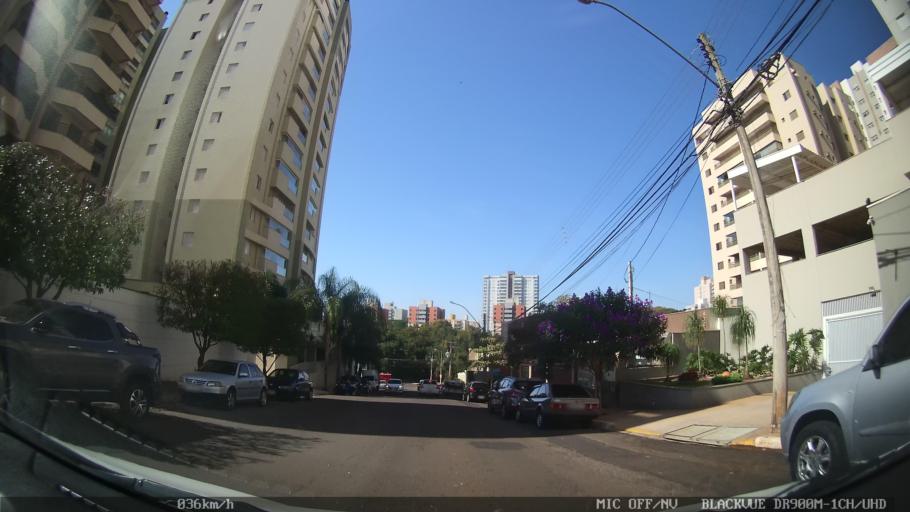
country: BR
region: Sao Paulo
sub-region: Ribeirao Preto
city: Ribeirao Preto
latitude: -21.2092
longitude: -47.7951
